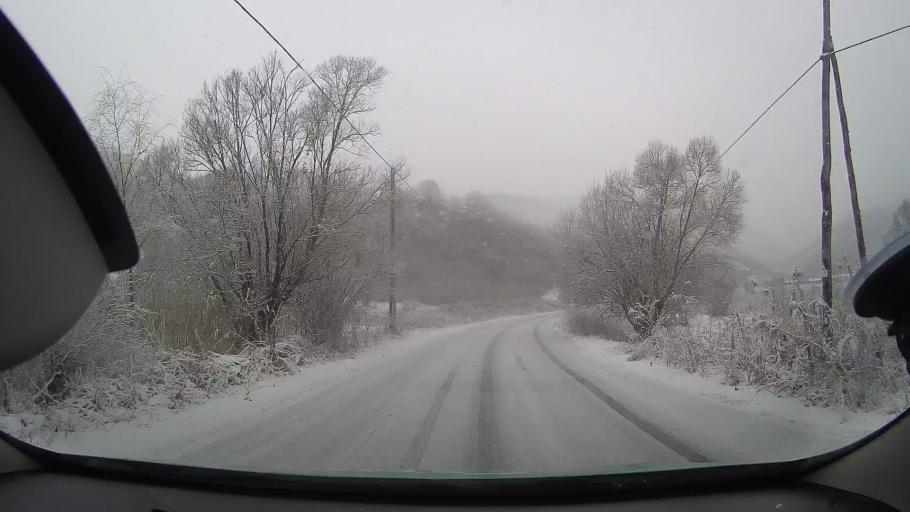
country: RO
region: Cluj
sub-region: Comuna Moldovenesti
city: Moldovenesti
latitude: 46.5025
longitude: 23.6061
